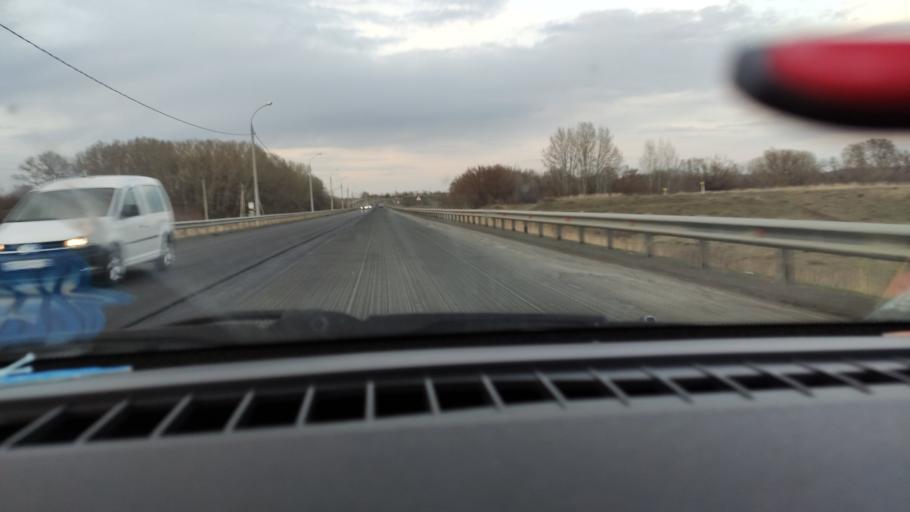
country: RU
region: Saratov
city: Yelshanka
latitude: 51.8255
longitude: 46.2212
